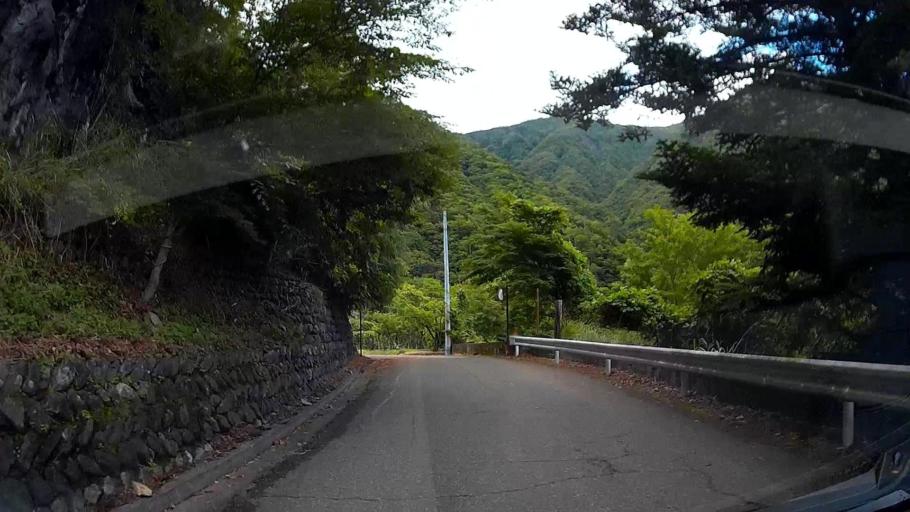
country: JP
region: Shizuoka
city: Shizuoka-shi
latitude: 35.3200
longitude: 138.1826
